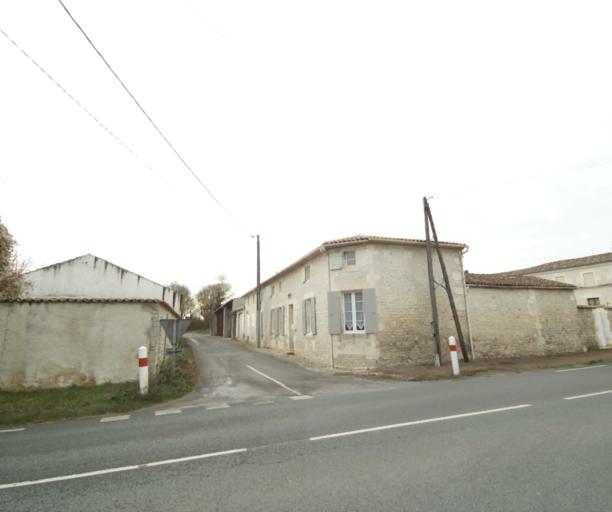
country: FR
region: Poitou-Charentes
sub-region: Departement de la Charente-Maritime
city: Corme-Royal
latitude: 45.7390
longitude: -0.8257
